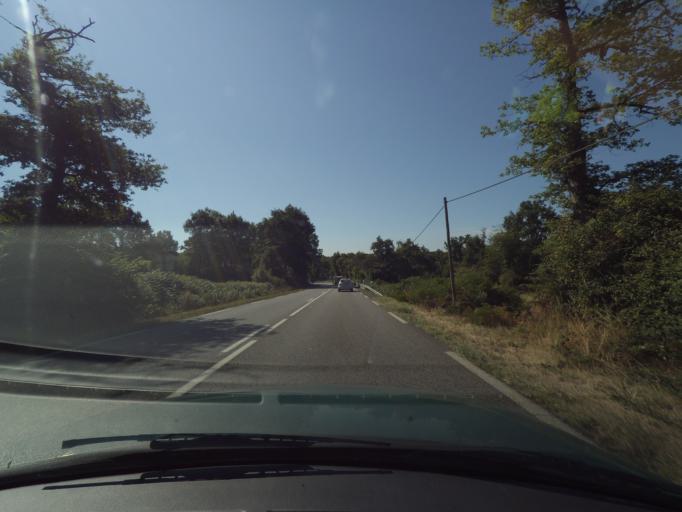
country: FR
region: Limousin
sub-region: Departement de la Haute-Vienne
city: Bellac
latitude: 46.1026
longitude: 1.0751
